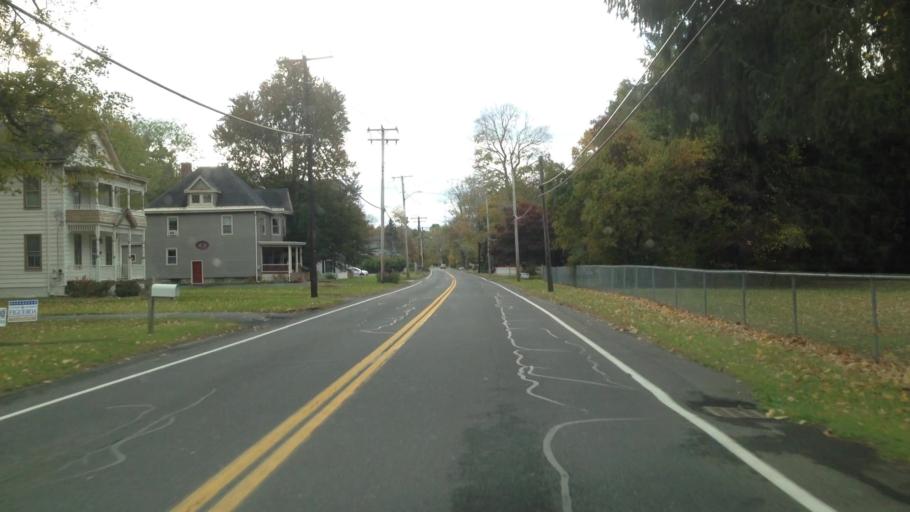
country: US
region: New York
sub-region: Ulster County
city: Tillson
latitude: 41.8316
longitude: -74.0771
